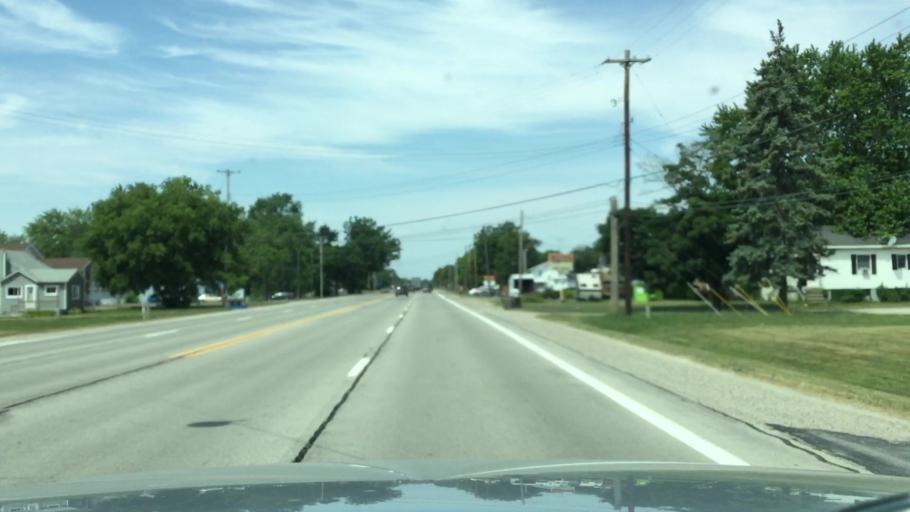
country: US
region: Michigan
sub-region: Genesee County
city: Swartz Creek
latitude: 43.0017
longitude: -83.7968
